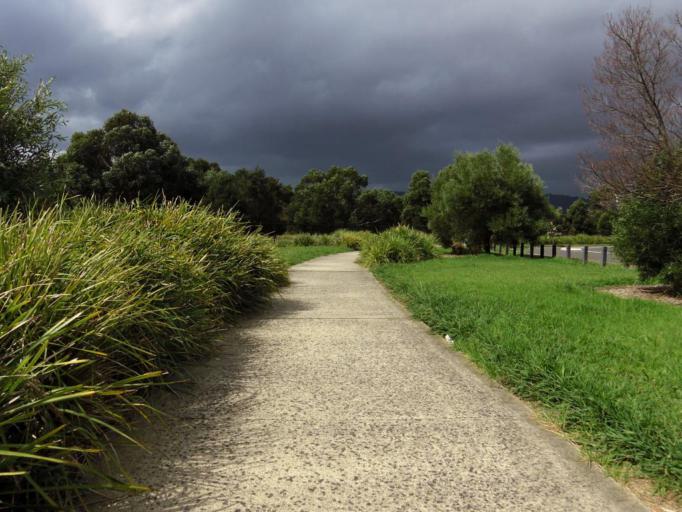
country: AU
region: Victoria
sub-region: Knox
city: Ferntree Gully
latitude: -37.9005
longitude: 145.2762
